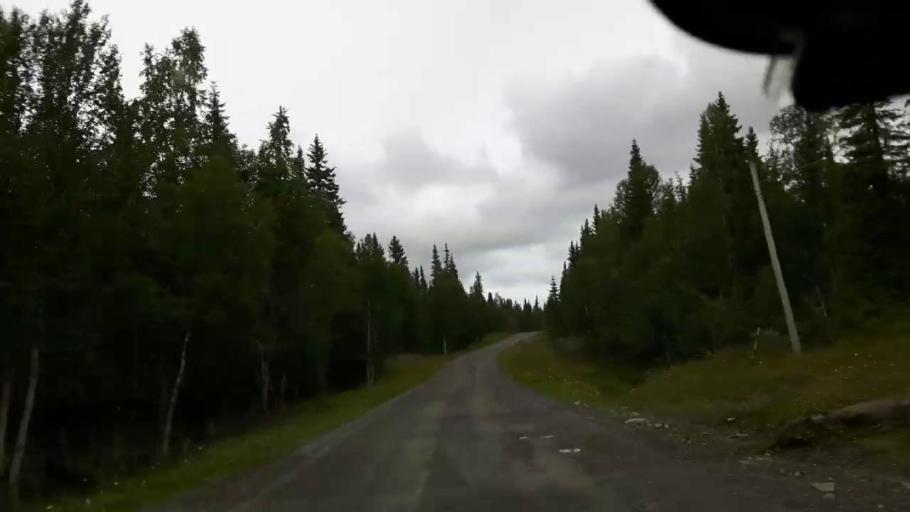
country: SE
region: Jaemtland
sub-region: Krokoms Kommun
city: Valla
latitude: 63.7523
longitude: 13.8356
